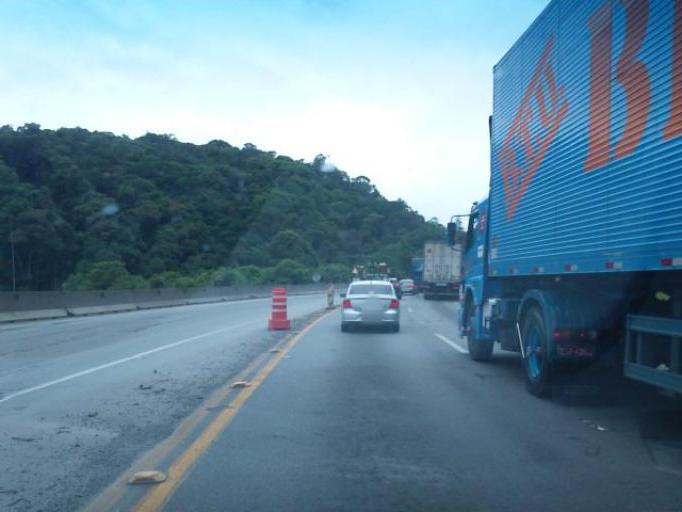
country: BR
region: Sao Paulo
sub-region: Juquitiba
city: Juquitiba
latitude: -24.0515
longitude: -47.2118
